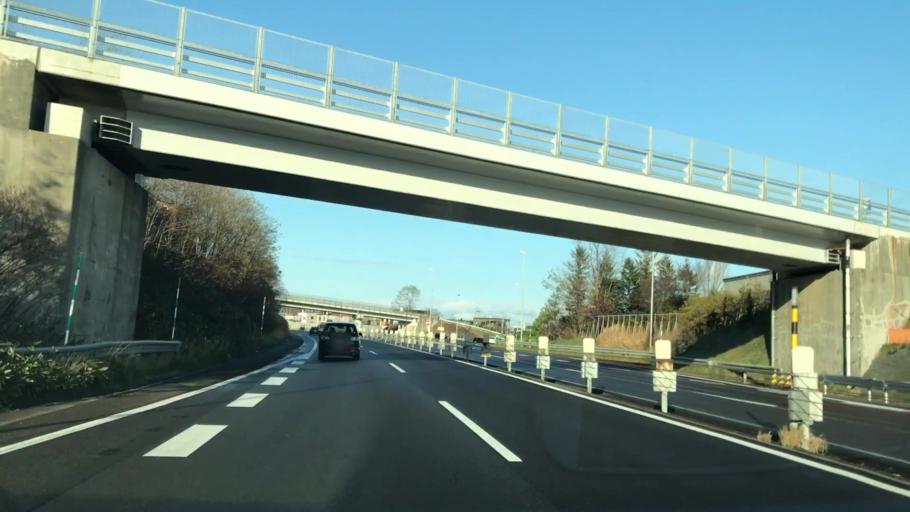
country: JP
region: Hokkaido
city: Sapporo
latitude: 43.1239
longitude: 141.2126
